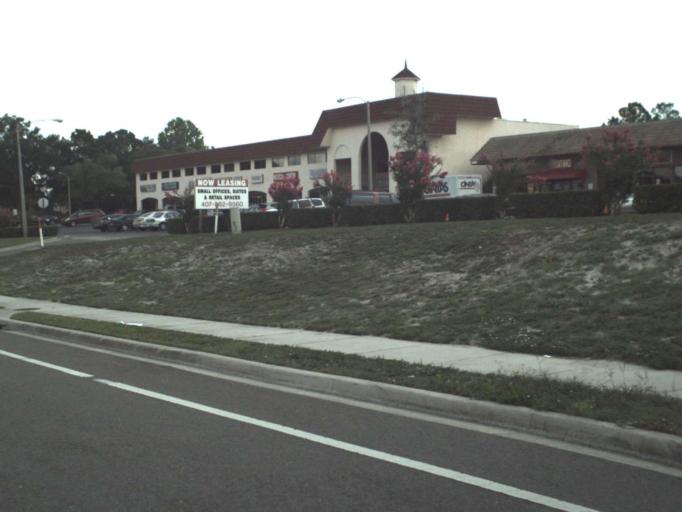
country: US
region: Florida
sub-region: Seminole County
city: Forest City
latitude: 28.6677
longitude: -81.4190
